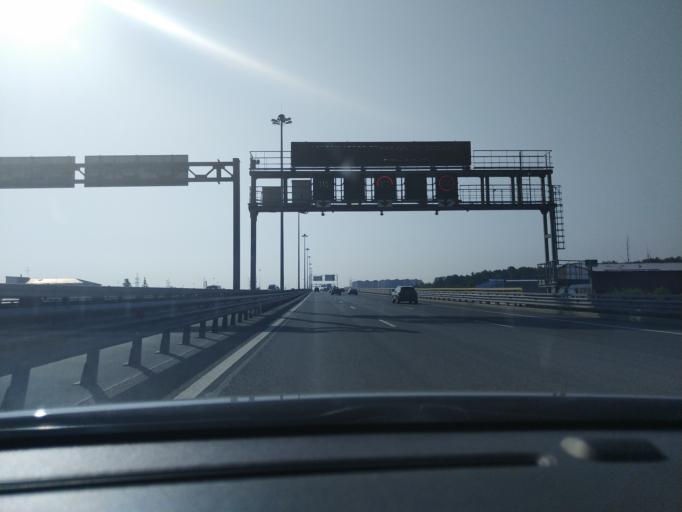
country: RU
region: St.-Petersburg
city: Sosnovaya Polyana
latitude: 59.8041
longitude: 30.1412
